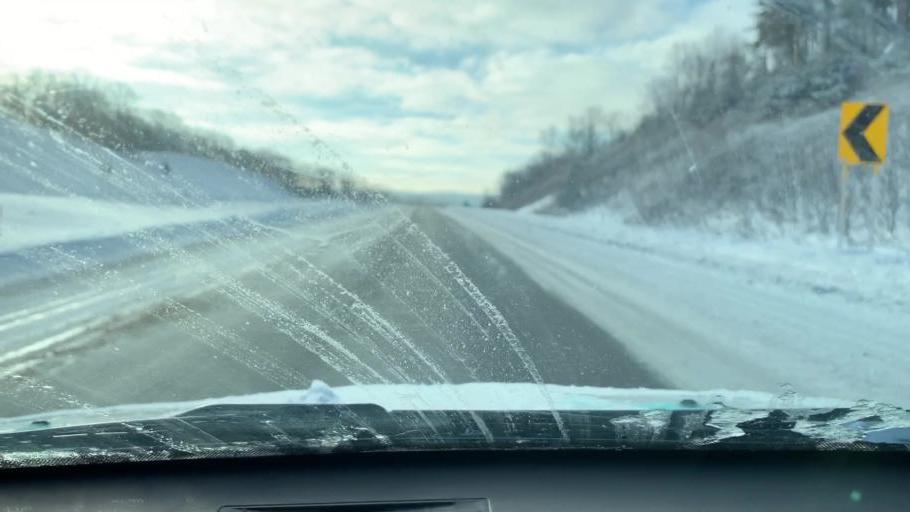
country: US
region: Michigan
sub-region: Wexford County
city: Cadillac
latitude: 44.2982
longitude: -85.3918
